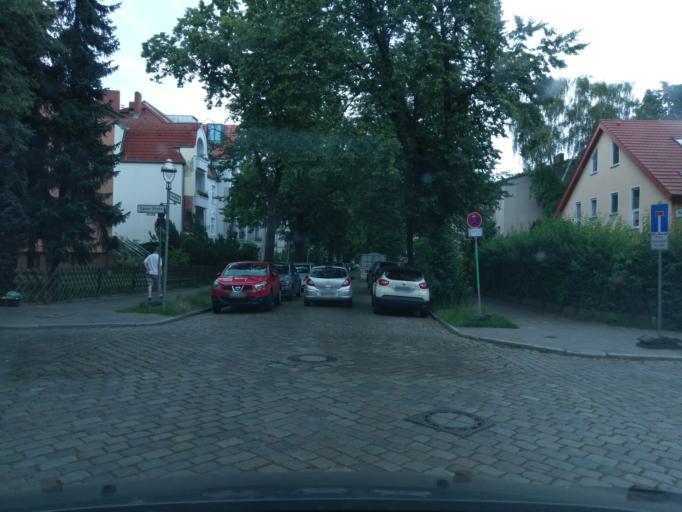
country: DE
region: Berlin
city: Lichterfelde
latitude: 52.4462
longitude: 13.3122
